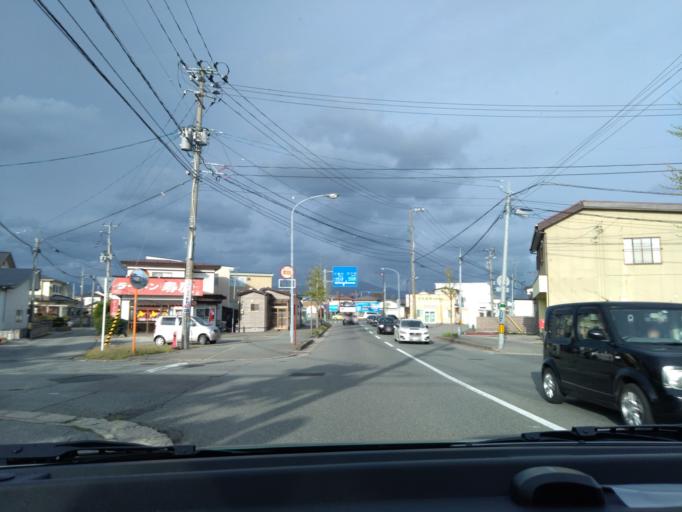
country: JP
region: Akita
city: Akita Shi
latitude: 39.7597
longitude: 140.0893
